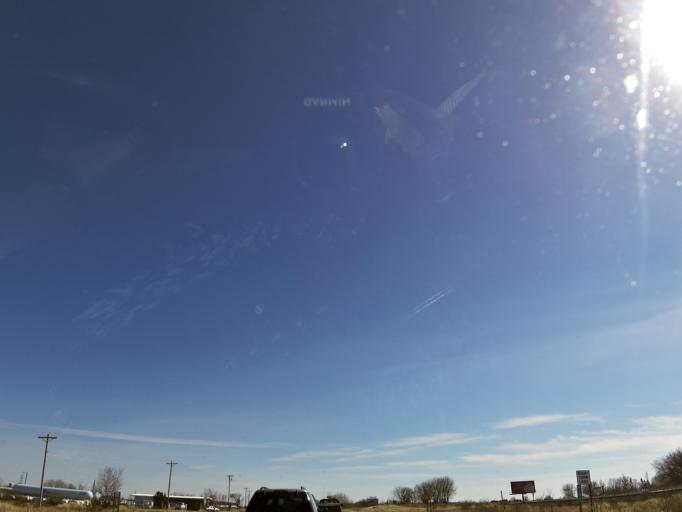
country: US
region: Minnesota
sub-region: Wright County
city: Buffalo
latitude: 45.1617
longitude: -93.8565
